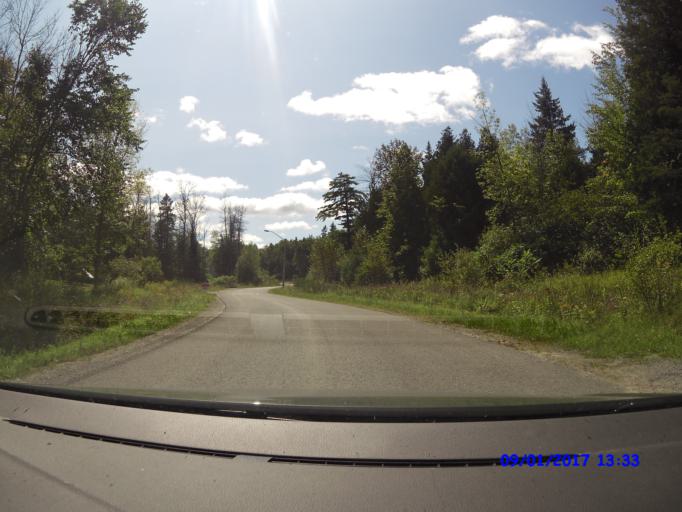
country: CA
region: Ontario
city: Bells Corners
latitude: 45.3539
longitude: -75.9975
